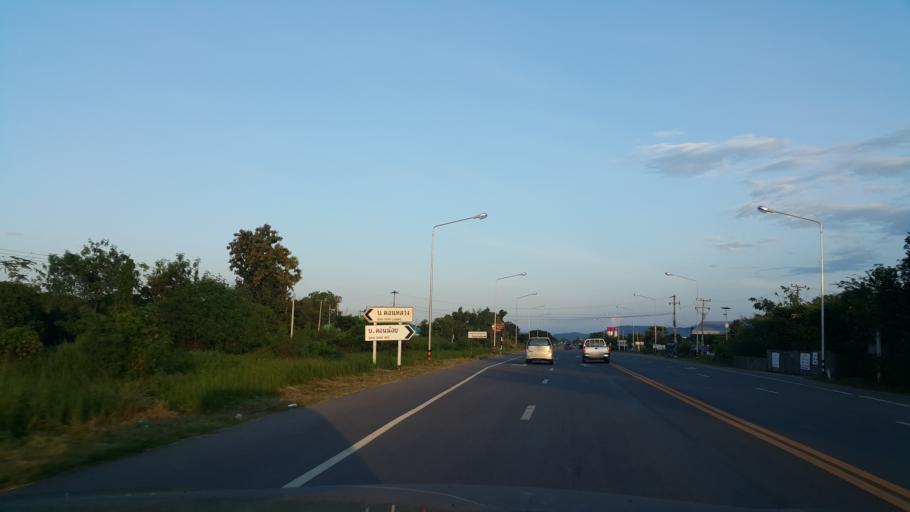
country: TH
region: Lamphun
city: Pa Sang
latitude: 18.4891
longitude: 98.9206
